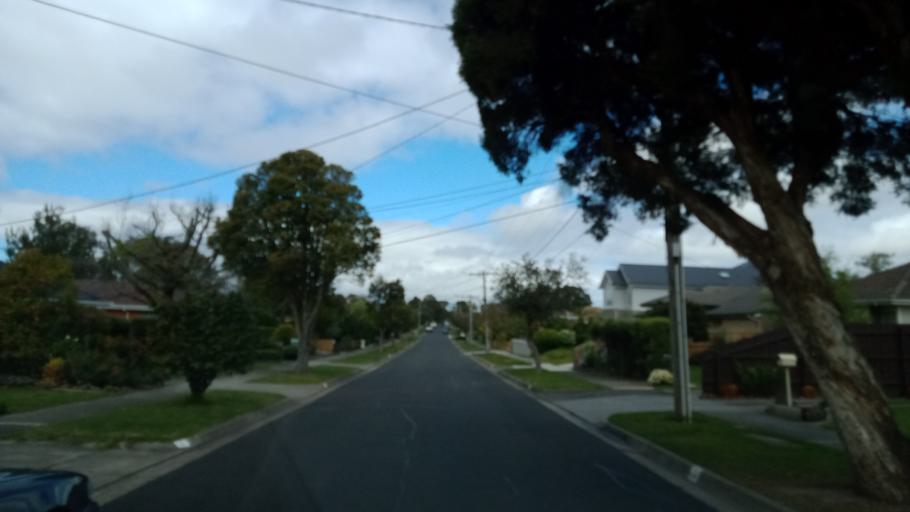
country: AU
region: Victoria
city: Burwood East
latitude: -37.8622
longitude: 145.1392
